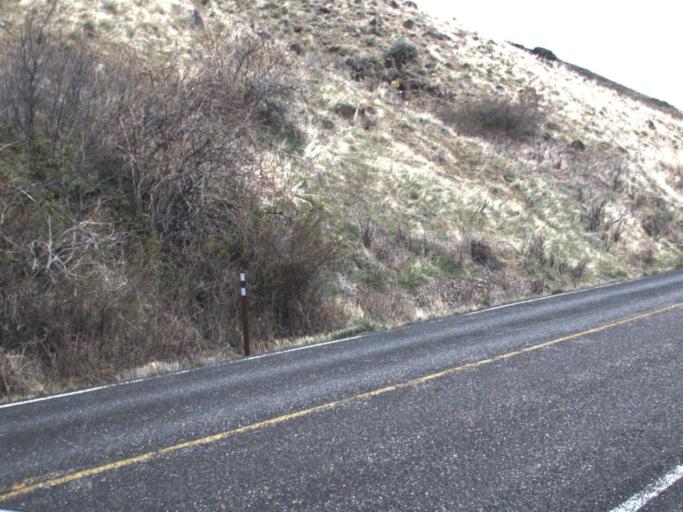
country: US
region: Washington
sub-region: Yakima County
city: Tieton
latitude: 46.7496
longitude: -120.8060
